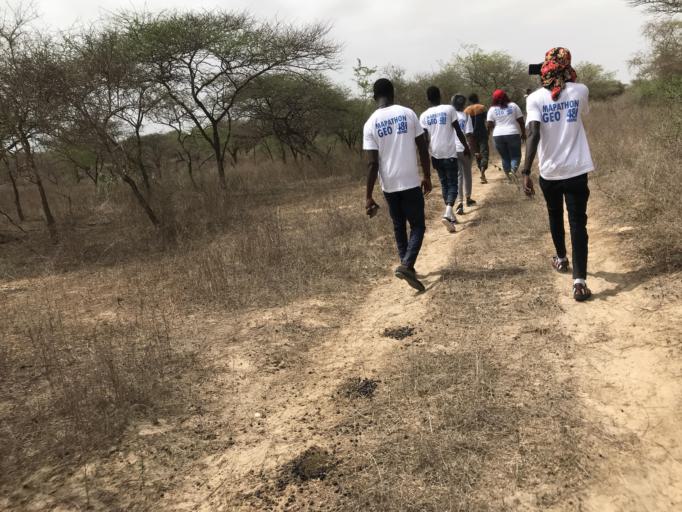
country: SN
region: Saint-Louis
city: Saint-Louis
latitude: 15.9124
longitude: -16.4555
